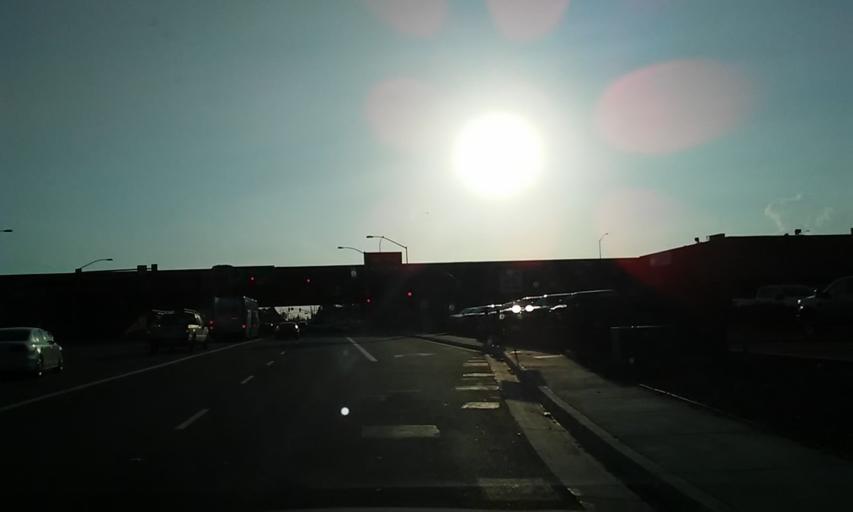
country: US
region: California
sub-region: San Bernardino County
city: San Bernardino
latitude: 34.1028
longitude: -117.3004
